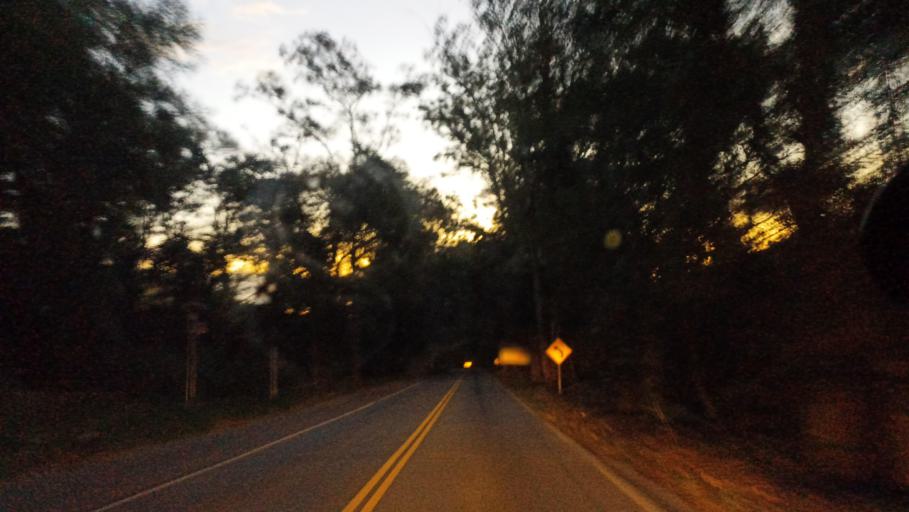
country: BR
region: Minas Gerais
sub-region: Sao Lourenco
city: Sao Lourenco
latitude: -22.1742
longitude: -44.9657
